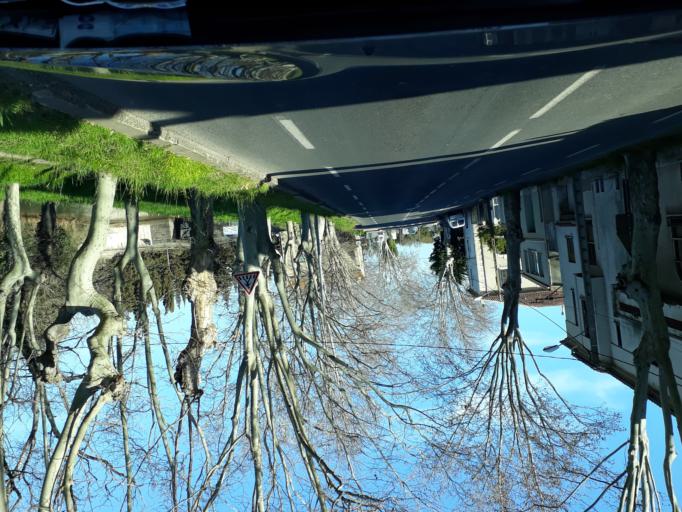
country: FR
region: Languedoc-Roussillon
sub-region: Departement de l'Herault
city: Agde
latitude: 43.3189
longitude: 3.4677
